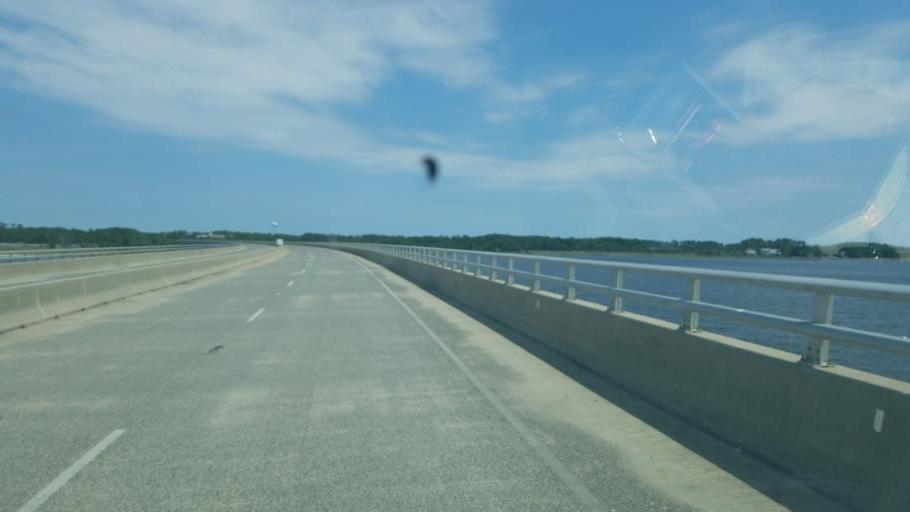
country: US
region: North Carolina
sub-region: Dare County
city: Manteo
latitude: 35.8819
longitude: -75.6800
